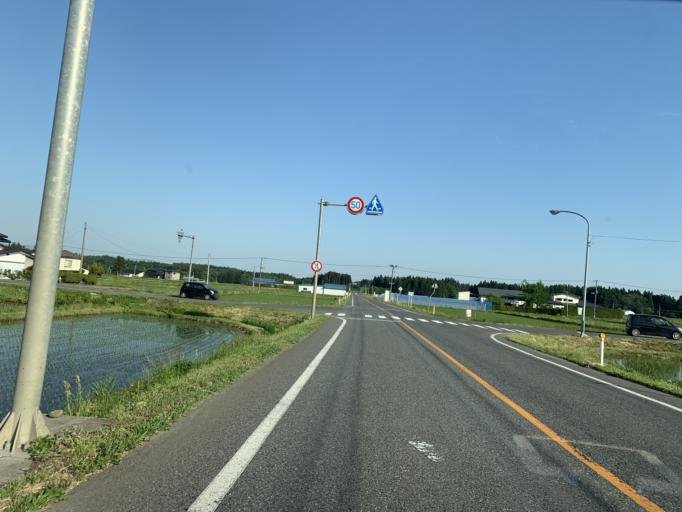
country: JP
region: Iwate
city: Mizusawa
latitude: 39.1680
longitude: 141.0458
